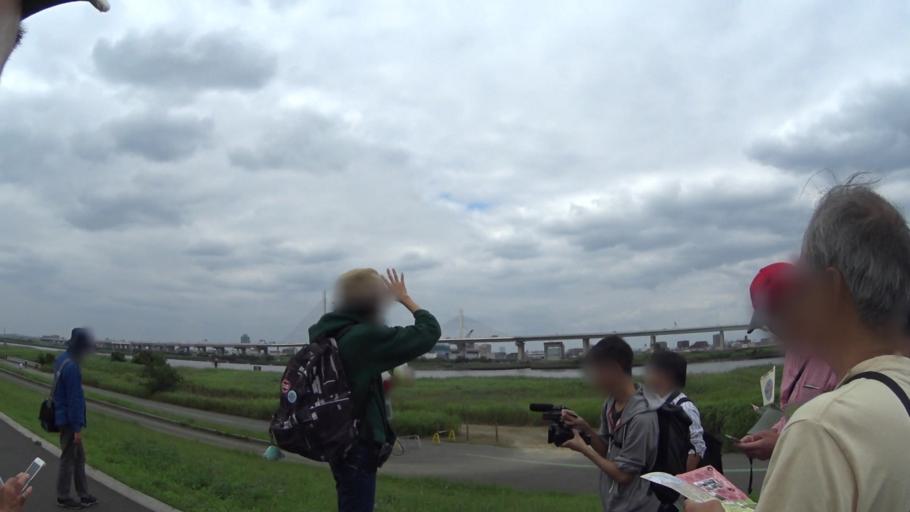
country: JP
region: Tokyo
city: Urayasu
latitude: 35.7165
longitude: 139.8414
